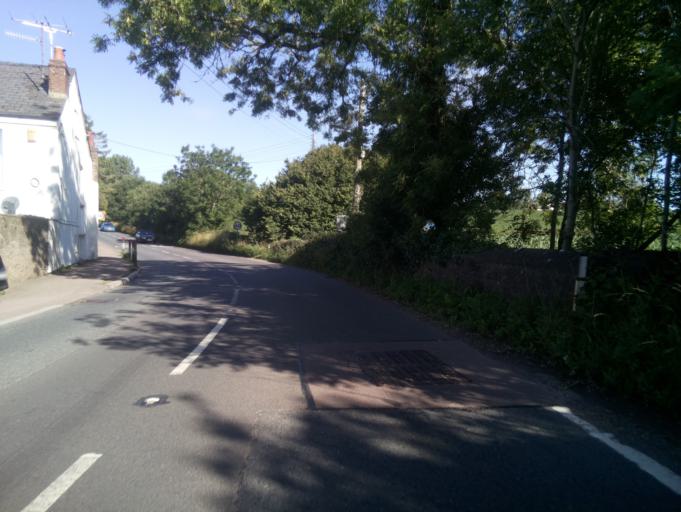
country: GB
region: England
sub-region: Gloucestershire
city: Coleford
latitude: 51.7993
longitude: -2.6251
